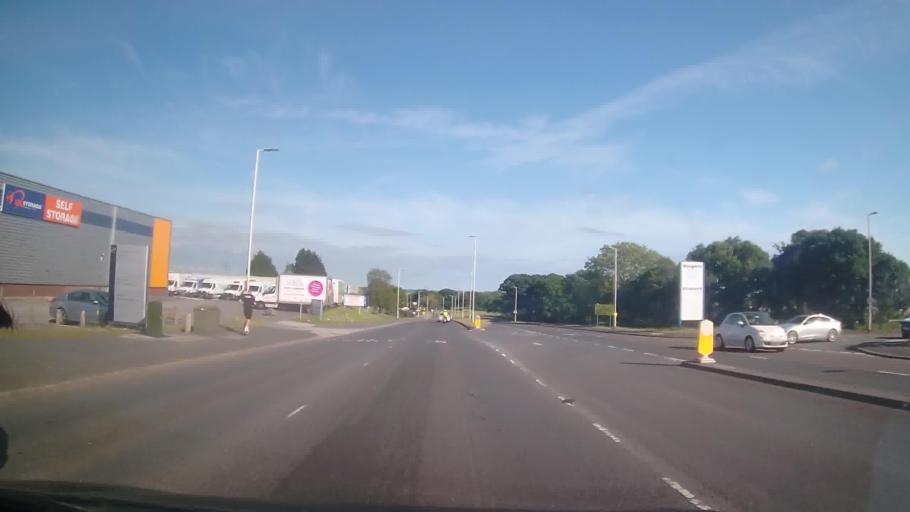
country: GB
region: England
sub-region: Devon
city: Plympton
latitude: 50.4190
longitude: -4.0926
